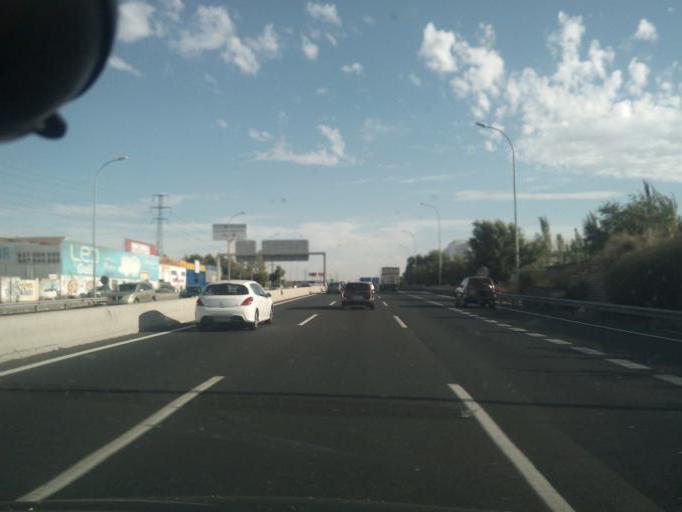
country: ES
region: Madrid
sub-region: Provincia de Madrid
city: Pinto
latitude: 40.2430
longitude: -3.6898
